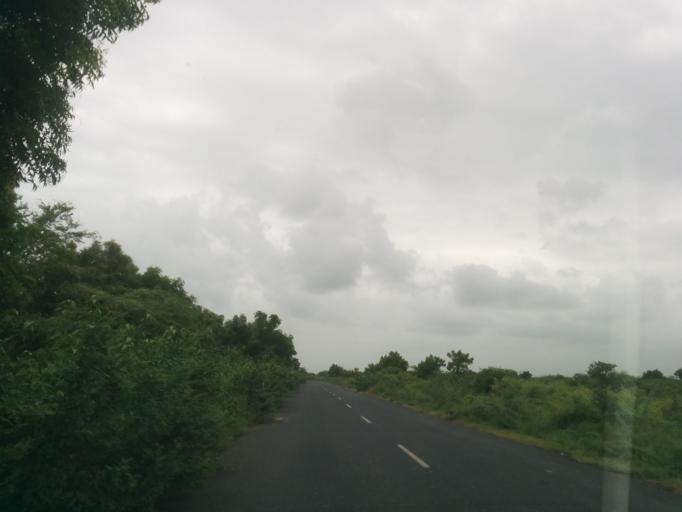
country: IN
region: Gujarat
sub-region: Ahmadabad
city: Sanand
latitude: 23.0780
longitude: 72.4013
